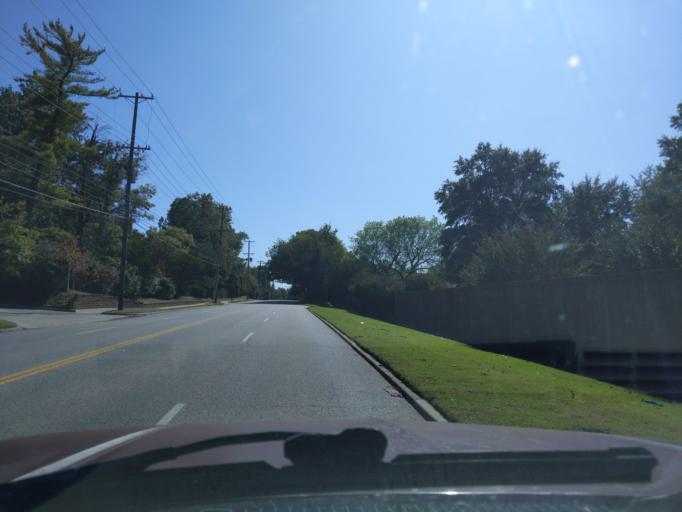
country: US
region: Oklahoma
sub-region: Tulsa County
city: Tulsa
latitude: 36.1096
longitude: -95.9581
